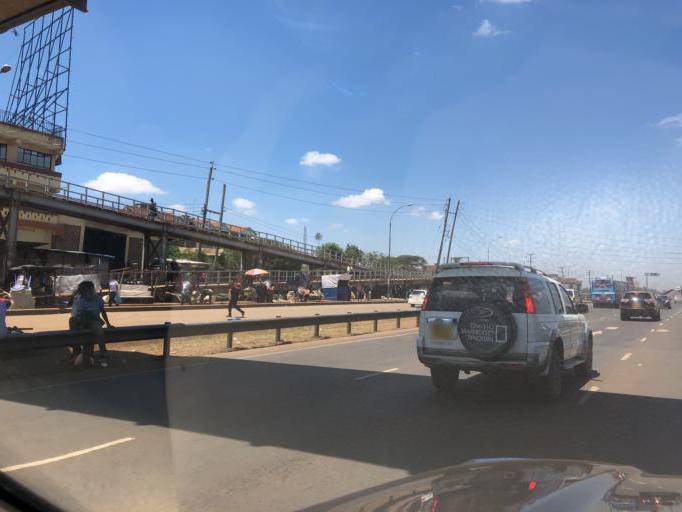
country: KE
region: Kiambu
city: Kiambu
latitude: -1.2169
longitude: 36.8946
